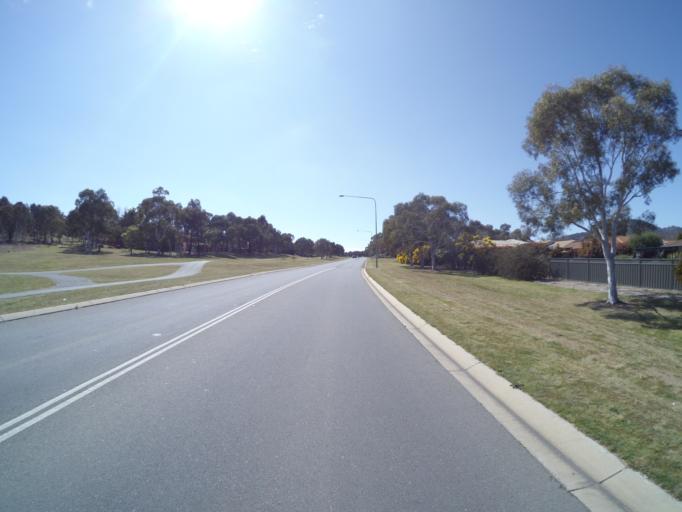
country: AU
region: Australian Capital Territory
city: Macarthur
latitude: -35.4443
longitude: 149.0811
